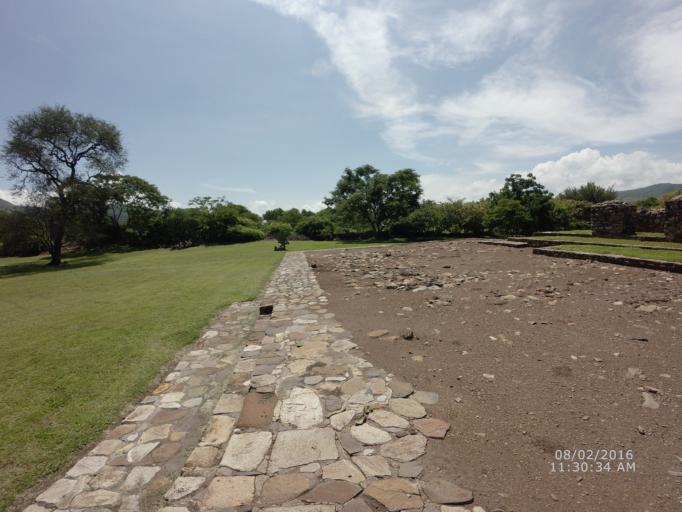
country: MX
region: Nayarit
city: Ixtlan del Rio
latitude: 21.0399
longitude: -104.3442
